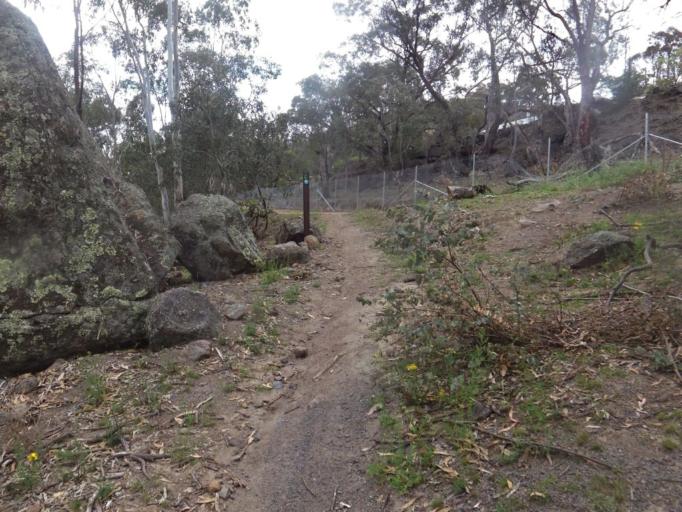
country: AU
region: Australian Capital Territory
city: Forrest
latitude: -35.3547
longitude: 149.1245
